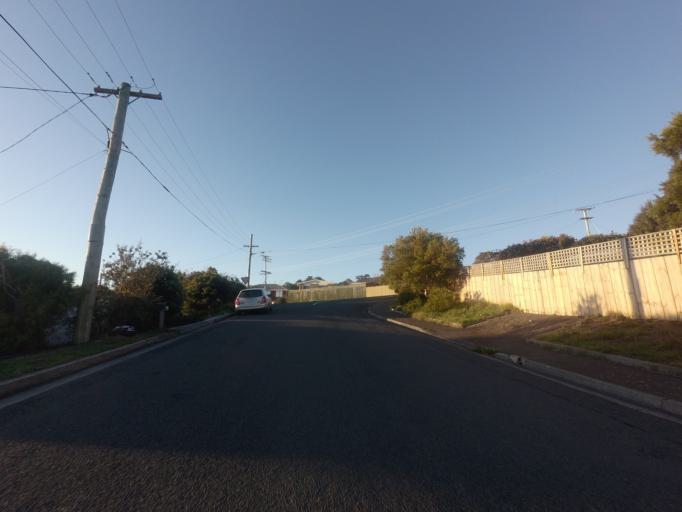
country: AU
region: Tasmania
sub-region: Sorell
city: Sorell
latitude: -42.7977
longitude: 147.5267
